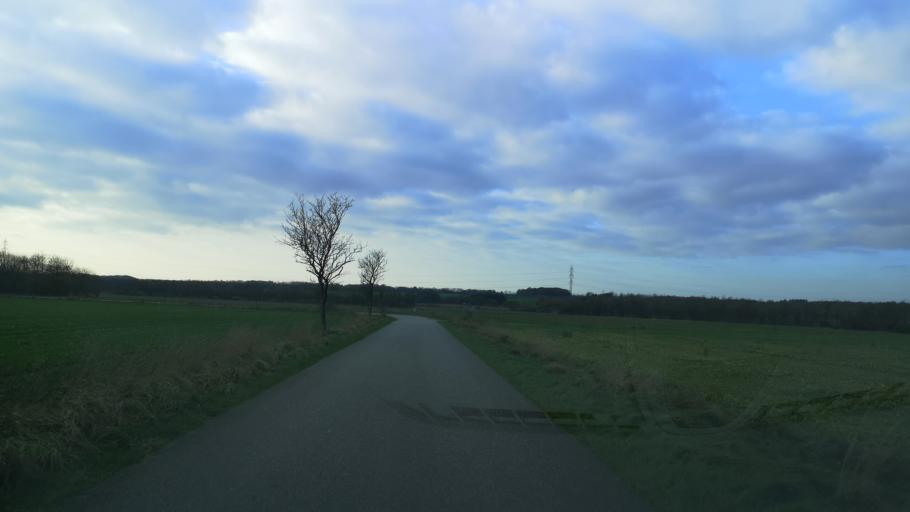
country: DK
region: Central Jutland
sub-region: Ringkobing-Skjern Kommune
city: Videbaek
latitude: 56.0077
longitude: 8.5953
